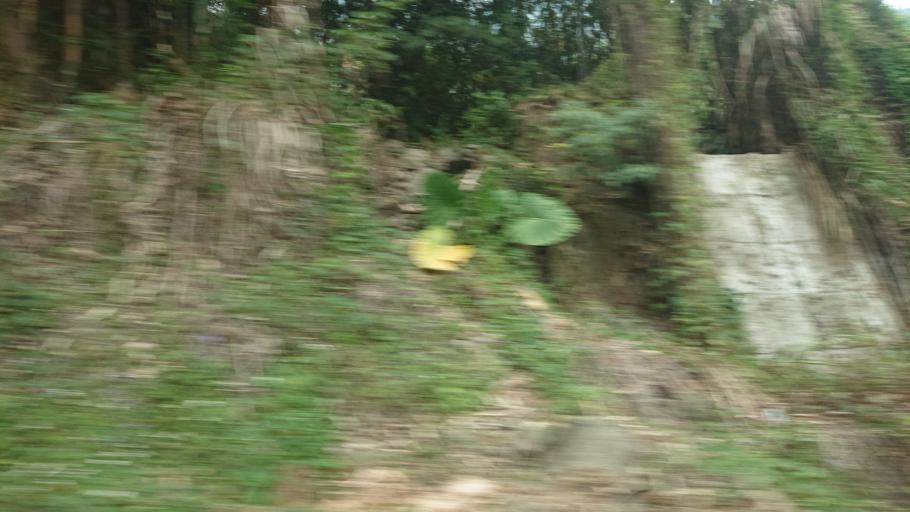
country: TW
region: Taiwan
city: Lugu
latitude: 23.5987
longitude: 120.6991
